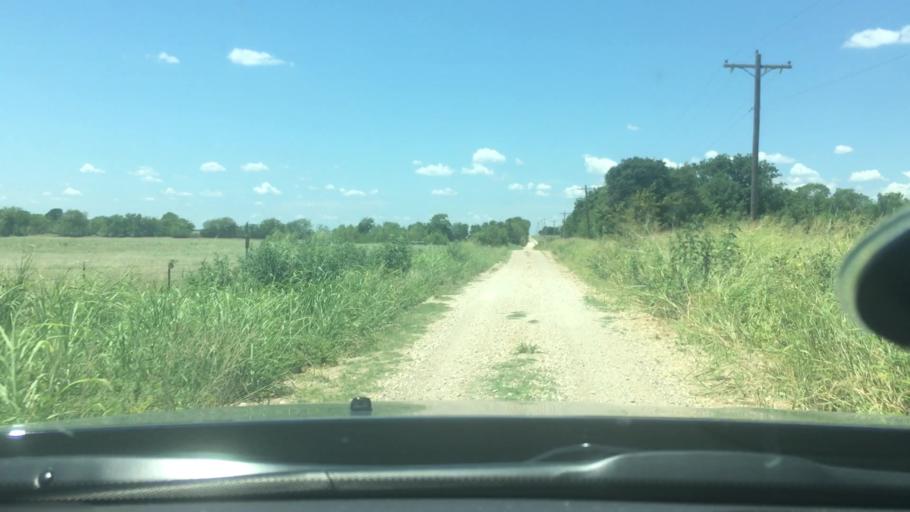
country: US
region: Oklahoma
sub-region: Bryan County
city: Durant
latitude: 33.9972
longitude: -96.0996
